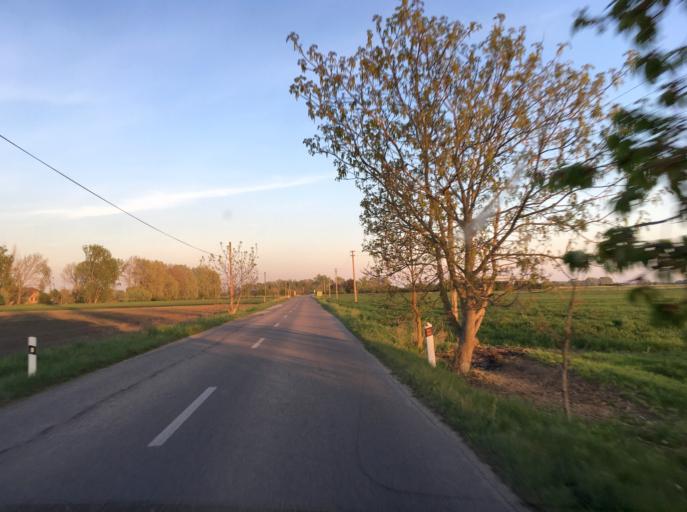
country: SK
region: Nitriansky
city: Kolarovo
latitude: 47.8865
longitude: 17.8994
